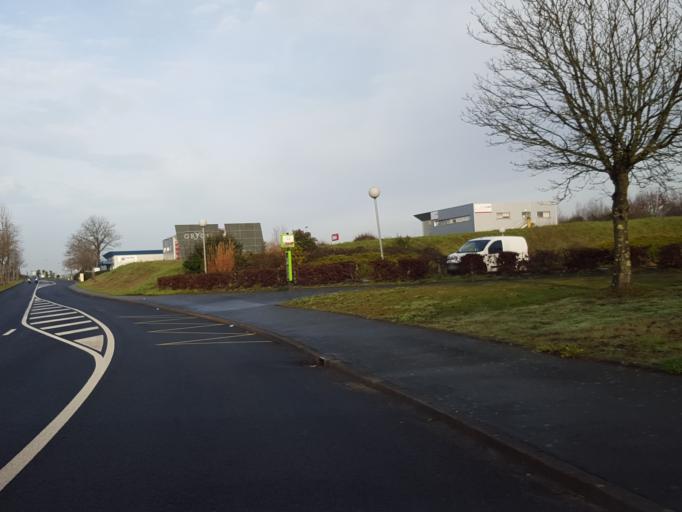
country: FR
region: Pays de la Loire
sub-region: Departement de la Vendee
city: La Roche-sur-Yon
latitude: 46.6776
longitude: -1.4061
